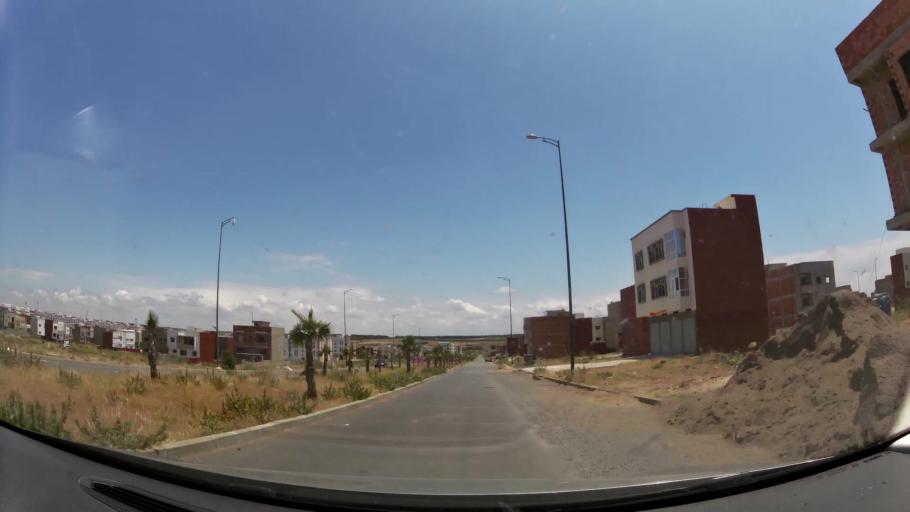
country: MA
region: Gharb-Chrarda-Beni Hssen
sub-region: Kenitra Province
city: Kenitra
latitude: 34.2478
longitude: -6.6590
